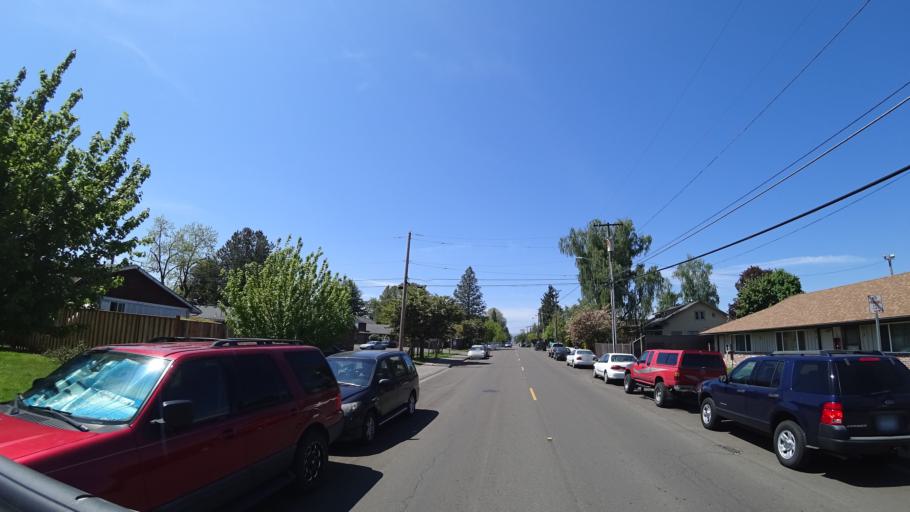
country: US
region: Oregon
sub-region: Washington County
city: Hillsboro
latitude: 45.5186
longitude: -122.9688
